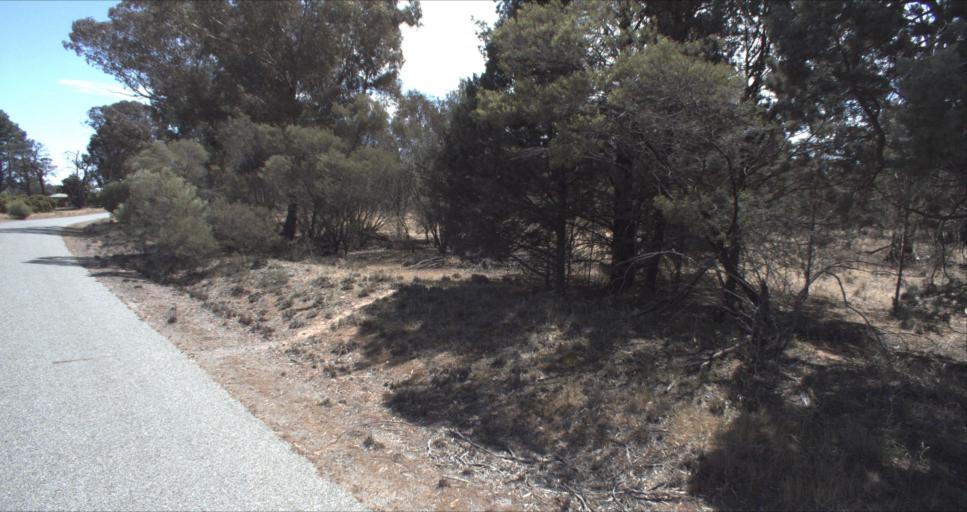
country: AU
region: New South Wales
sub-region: Leeton
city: Leeton
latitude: -34.6772
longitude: 146.4365
